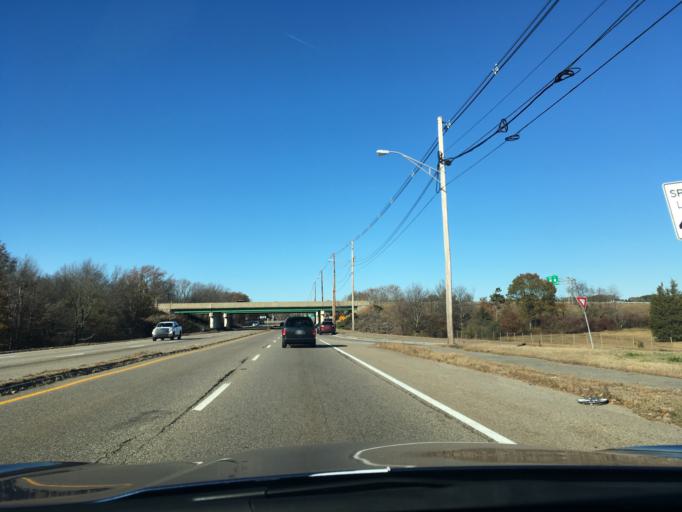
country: US
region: Massachusetts
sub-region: Bristol County
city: North Seekonk
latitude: 41.9008
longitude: -71.3555
